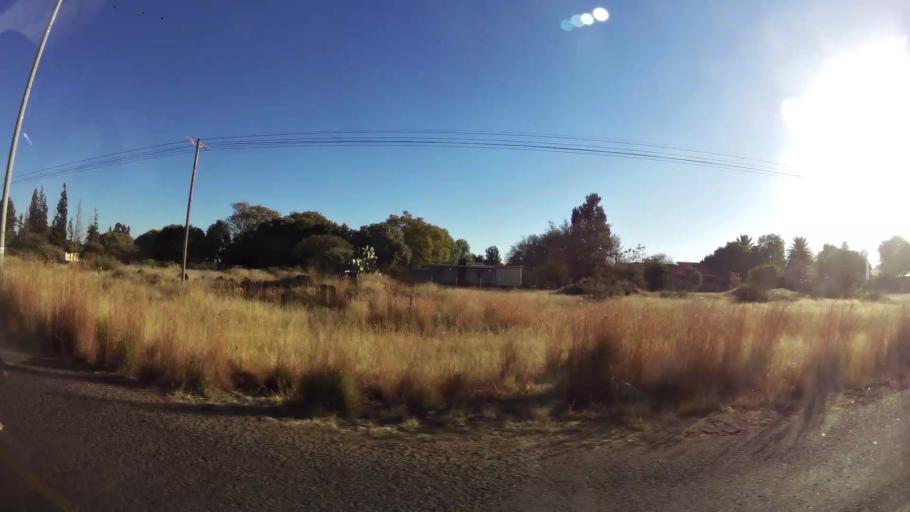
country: ZA
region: Northern Cape
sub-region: Frances Baard District Municipality
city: Kimberley
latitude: -28.7430
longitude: 24.7214
